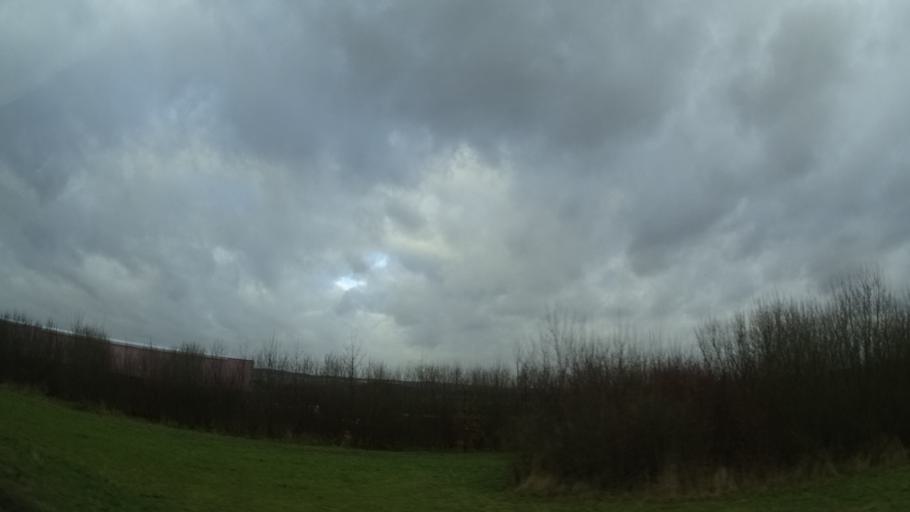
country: DE
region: Thuringia
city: Lemnitz
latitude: 50.7192
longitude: 11.8426
